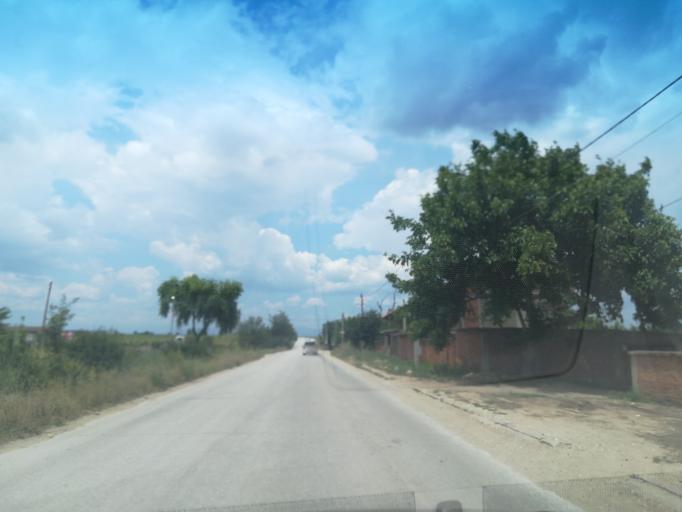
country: BG
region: Stara Zagora
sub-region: Obshtina Chirpan
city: Chirpan
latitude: 42.1779
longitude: 25.2072
